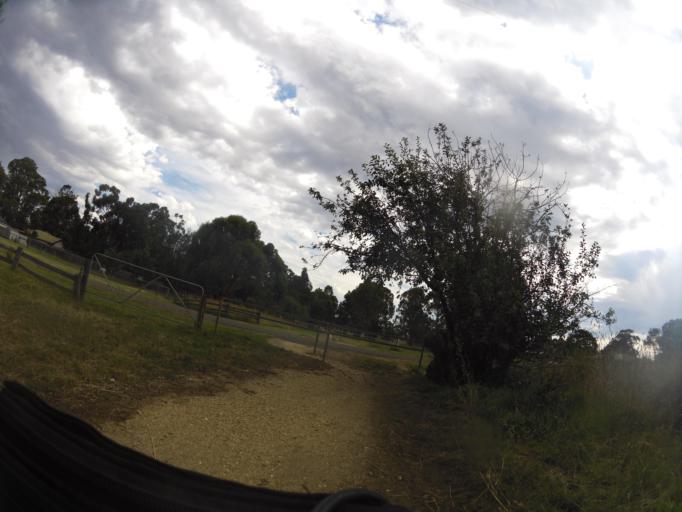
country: AU
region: Victoria
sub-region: Latrobe
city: Traralgon
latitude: -38.0536
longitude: 146.6279
